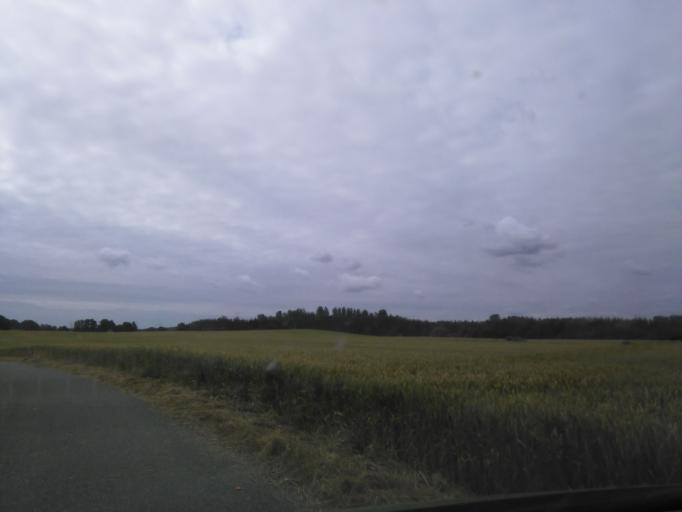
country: DK
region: Central Jutland
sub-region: Arhus Kommune
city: Solbjerg
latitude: 56.0377
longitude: 10.1243
